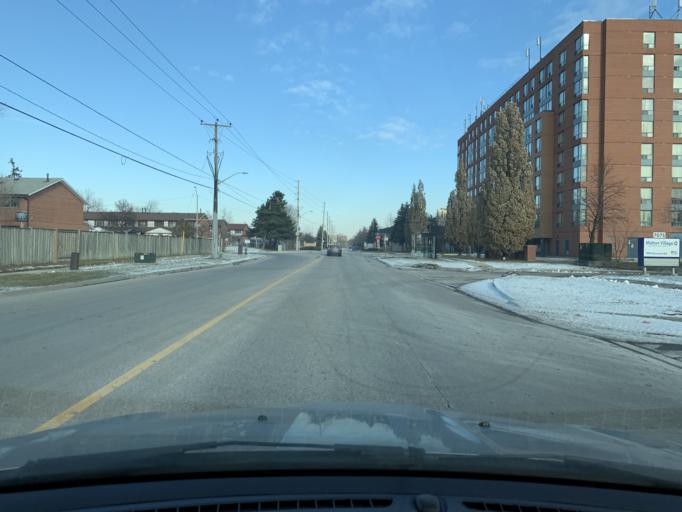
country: CA
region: Ontario
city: Etobicoke
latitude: 43.7185
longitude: -79.6262
